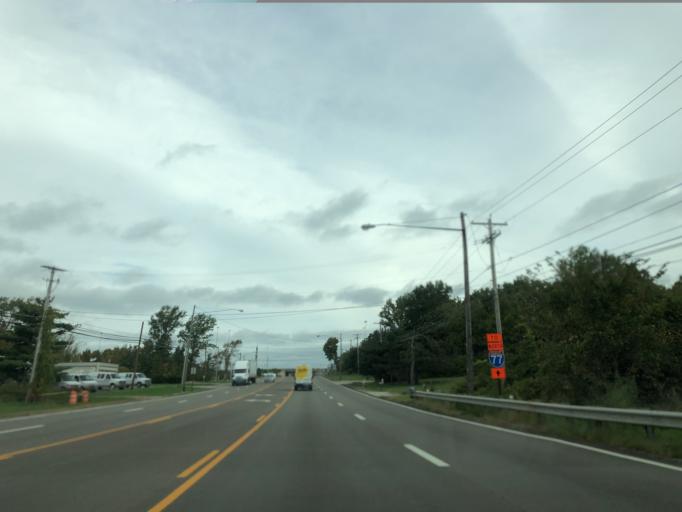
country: US
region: Ohio
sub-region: Summit County
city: Richfield
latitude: 41.2667
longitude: -81.6287
